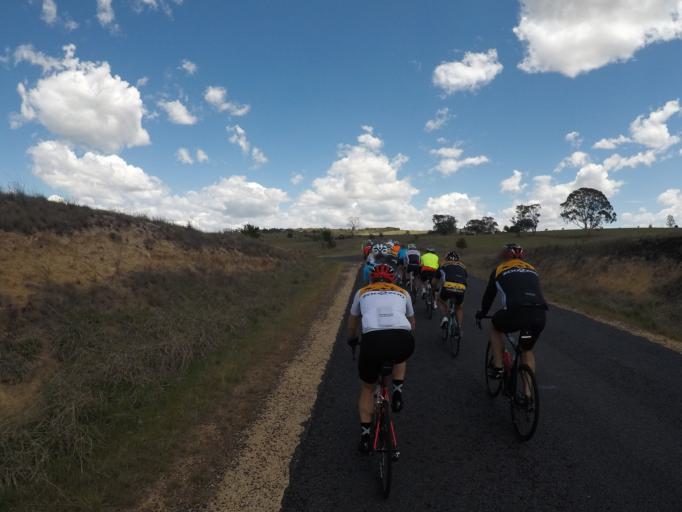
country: AU
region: New South Wales
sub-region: Bathurst Regional
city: Perthville
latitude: -33.5699
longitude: 149.4100
